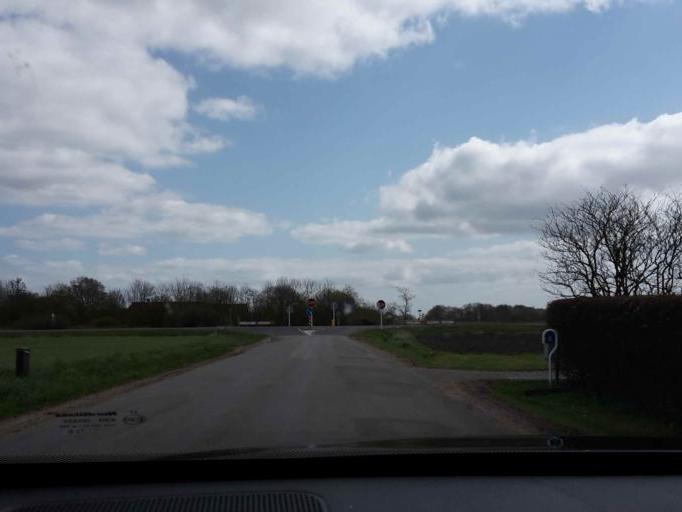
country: DK
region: South Denmark
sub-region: Varde Kommune
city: Olgod
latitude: 55.7769
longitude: 8.6222
